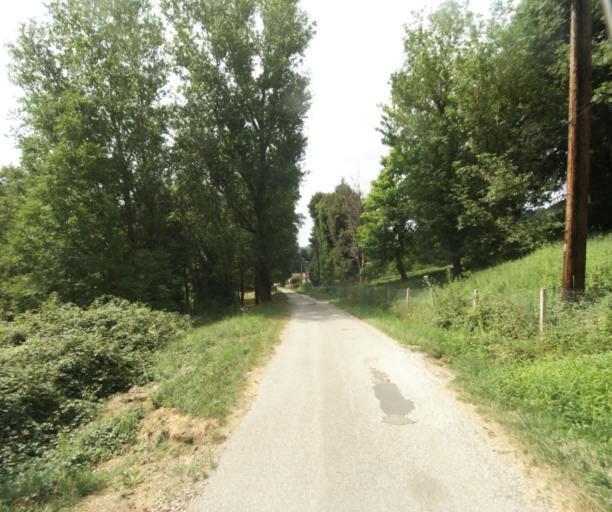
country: FR
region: Midi-Pyrenees
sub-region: Departement du Tarn
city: Soreze
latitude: 43.4325
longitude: 2.0426
